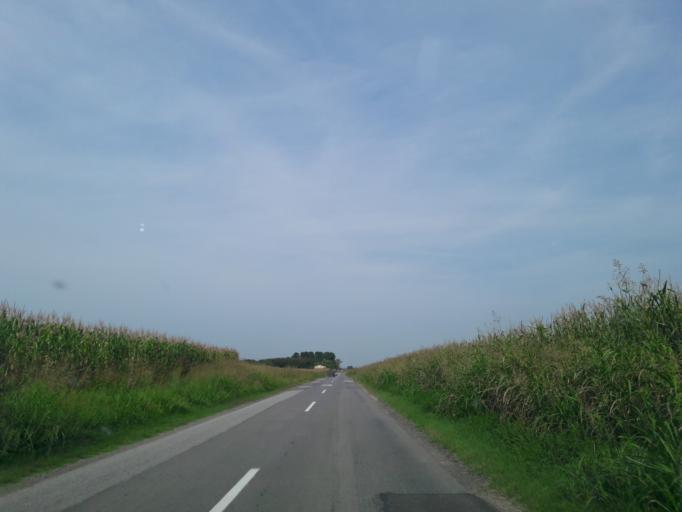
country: HR
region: Vukovarsko-Srijemska
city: Bobota
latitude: 45.4364
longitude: 18.8683
